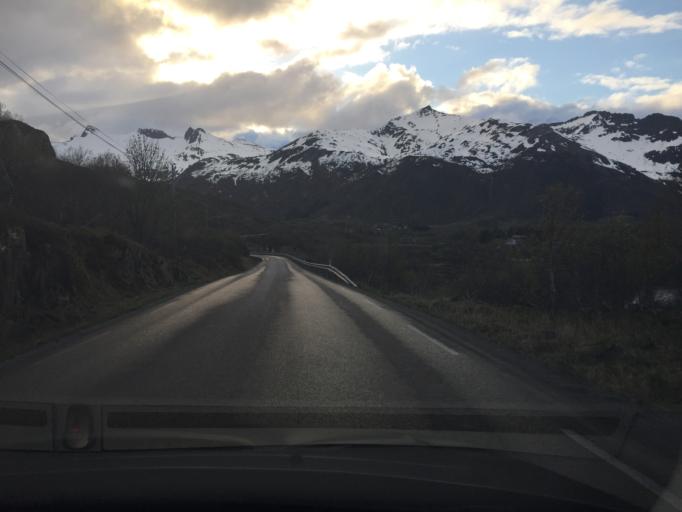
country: NO
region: Nordland
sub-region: Vagan
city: Svolvaer
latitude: 68.3167
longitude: 14.7135
